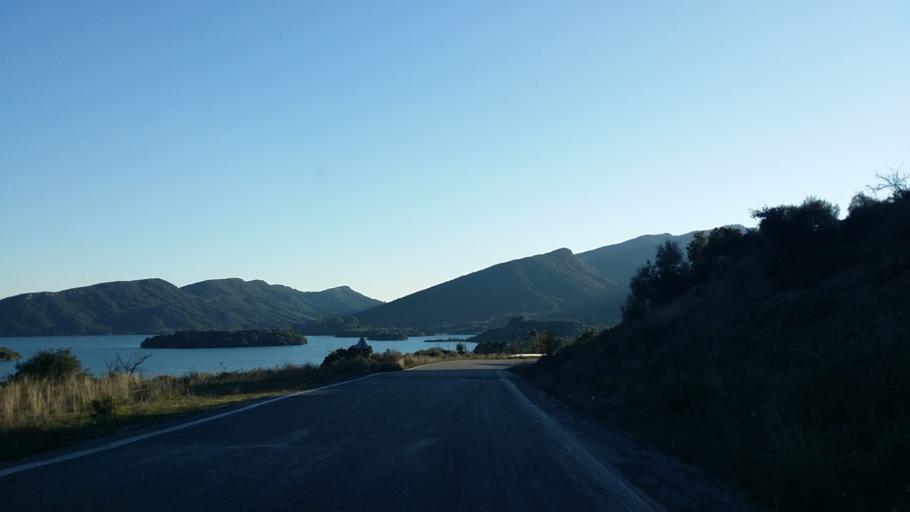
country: GR
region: West Greece
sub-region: Nomos Aitolias kai Akarnanias
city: Lepenou
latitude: 38.8398
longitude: 21.3314
